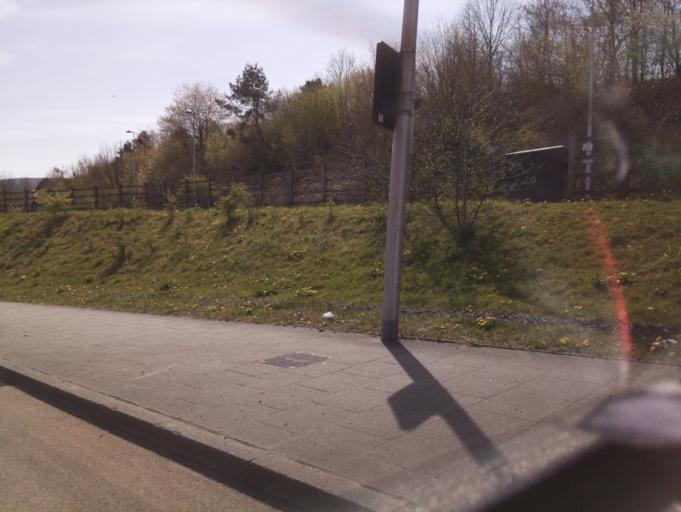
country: GB
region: Wales
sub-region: Merthyr Tydfil County Borough
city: Merthyr Tydfil
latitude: 51.7435
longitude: -3.3819
